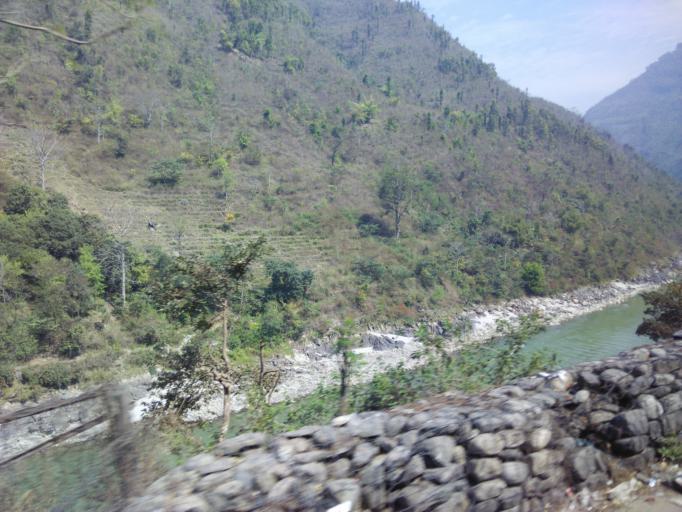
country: NP
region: Central Region
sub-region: Narayani Zone
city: Bharatpur
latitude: 27.8577
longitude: 84.5649
